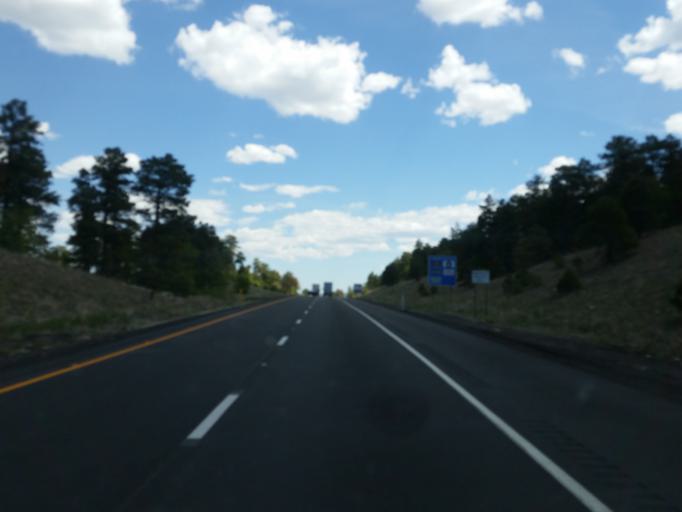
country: US
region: Arizona
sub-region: Coconino County
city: Williams
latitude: 35.2265
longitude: -112.2363
